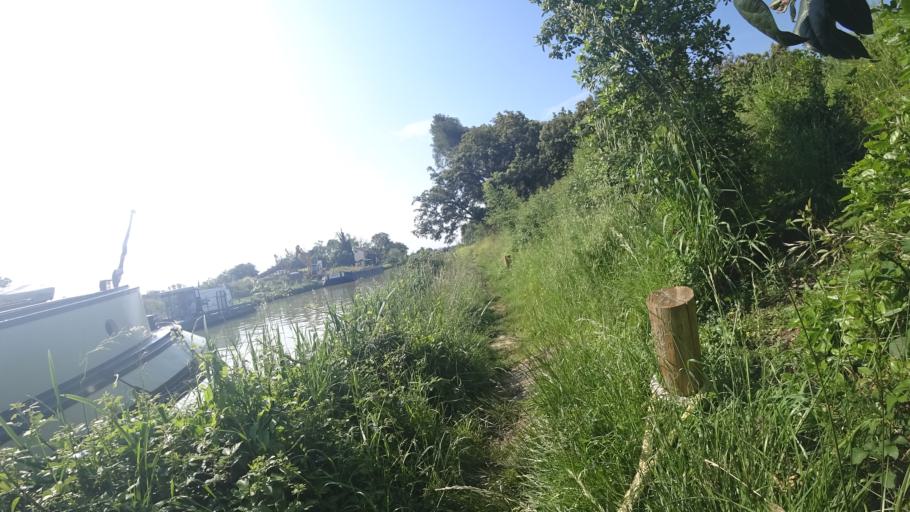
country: FR
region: Languedoc-Roussillon
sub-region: Departement de l'Aude
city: Argeliers
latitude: 43.2789
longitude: 2.9143
